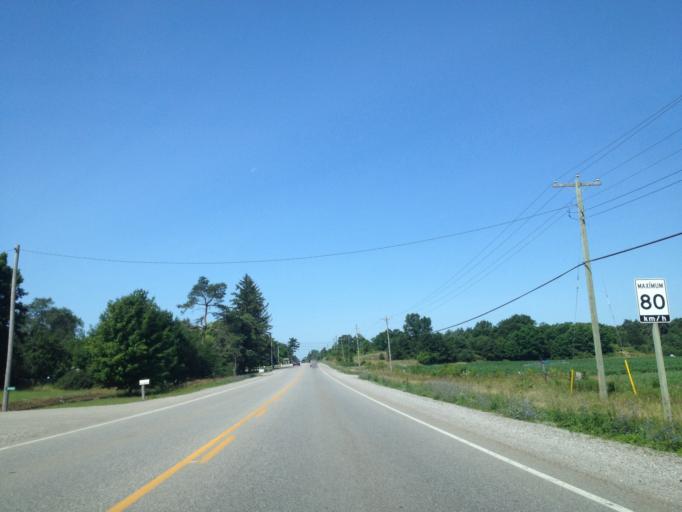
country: CA
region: Ontario
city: Norfolk County
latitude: 42.8370
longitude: -80.3560
